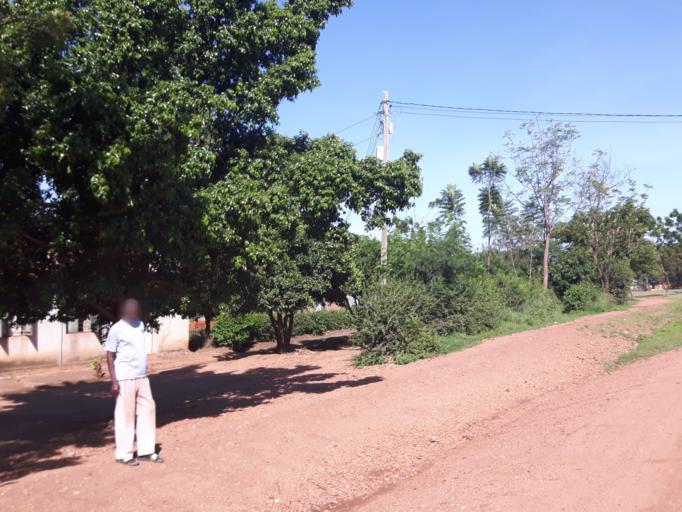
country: TZ
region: Mara
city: Issenye
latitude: -2.0250
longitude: 34.4521
